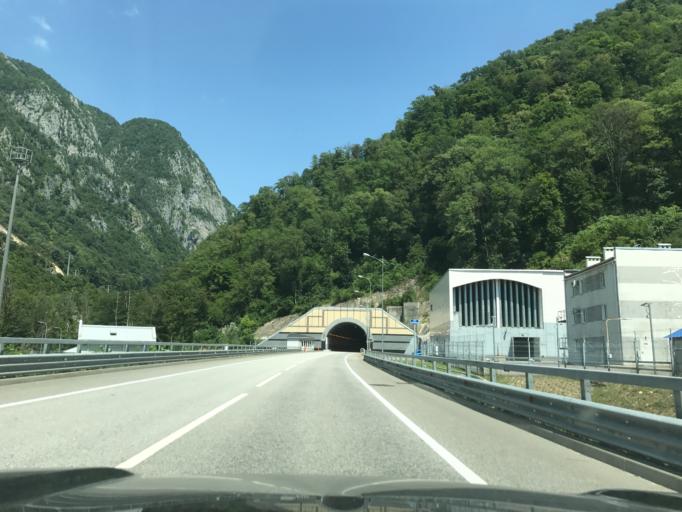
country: RU
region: Krasnodarskiy
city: Vysokoye
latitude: 43.5892
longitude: 40.0159
